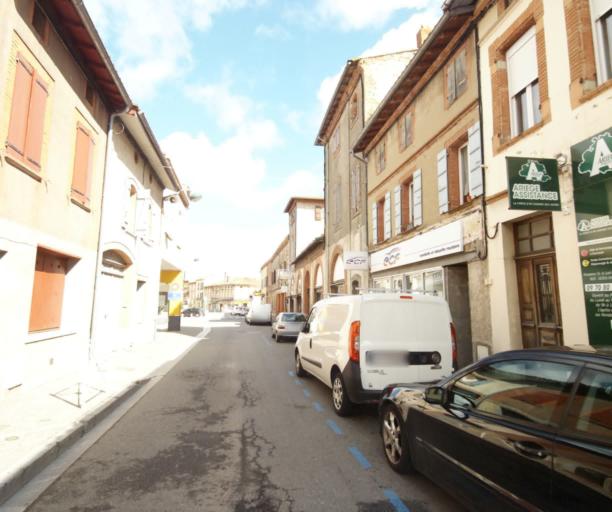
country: FR
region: Midi-Pyrenees
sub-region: Departement de l'Ariege
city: Saverdun
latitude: 43.2344
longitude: 1.5756
